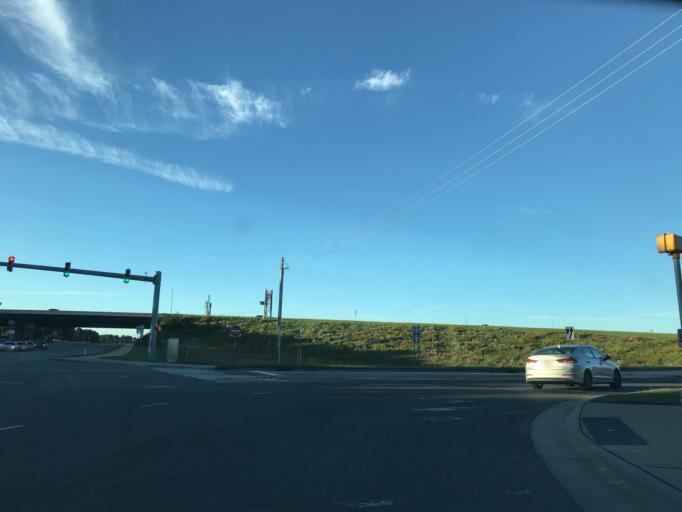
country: US
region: North Carolina
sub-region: Wake County
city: Morrisville
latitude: 35.8596
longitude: -78.8440
